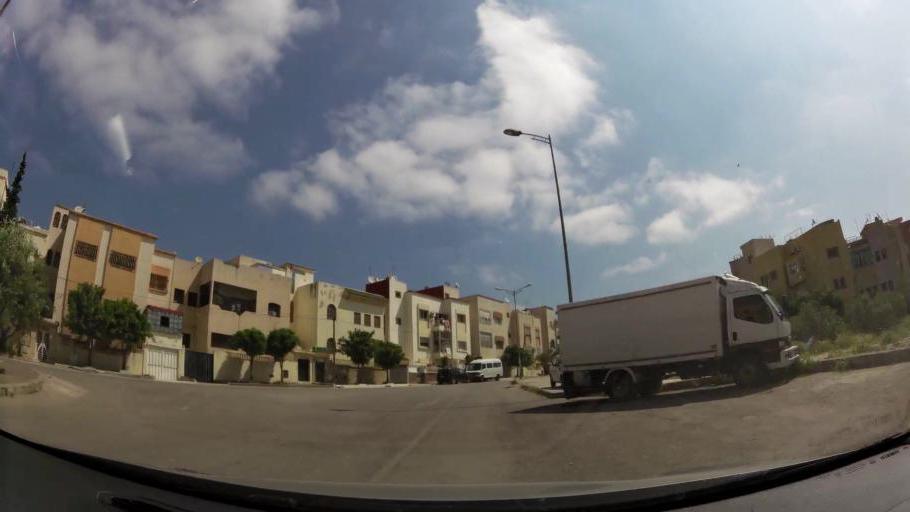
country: MA
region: Fes-Boulemane
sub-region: Fes
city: Fes
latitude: 34.0607
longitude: -5.0346
